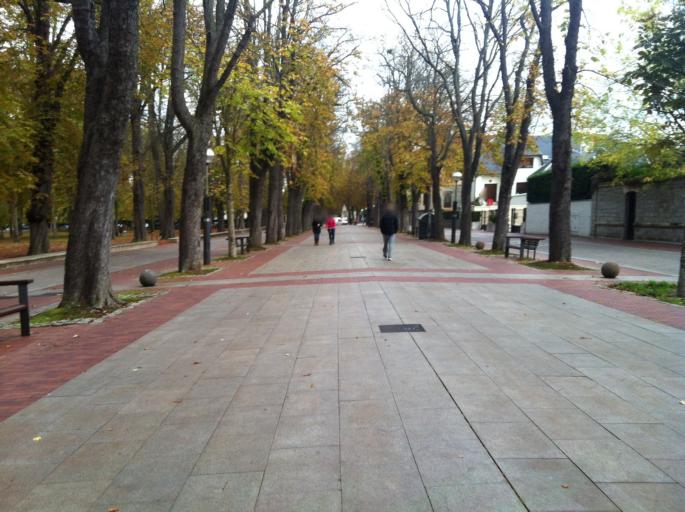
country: ES
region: Basque Country
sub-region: Provincia de Alava
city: Gasteiz / Vitoria
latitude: 42.8405
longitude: -2.6854
